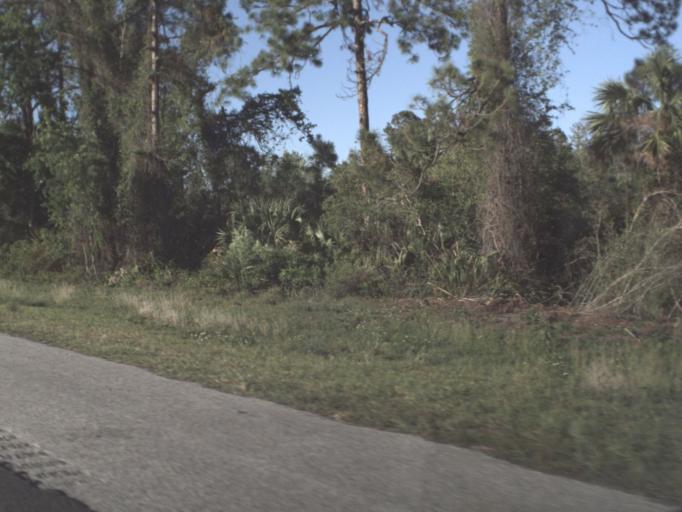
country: US
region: Florida
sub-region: Flagler County
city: Flagler Beach
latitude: 29.4332
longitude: -81.1674
